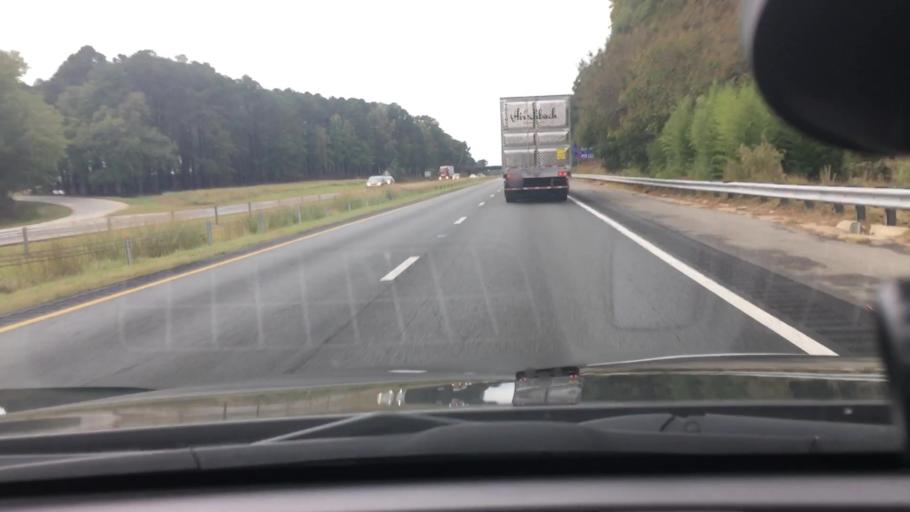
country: US
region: North Carolina
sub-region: Wake County
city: Apex
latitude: 35.7251
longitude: -78.8183
